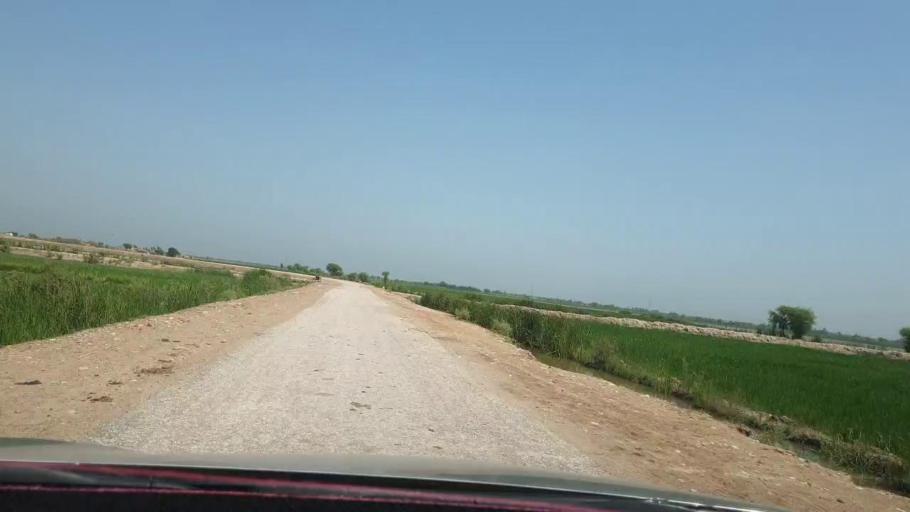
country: PK
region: Sindh
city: Warah
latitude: 27.5615
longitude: 67.7478
